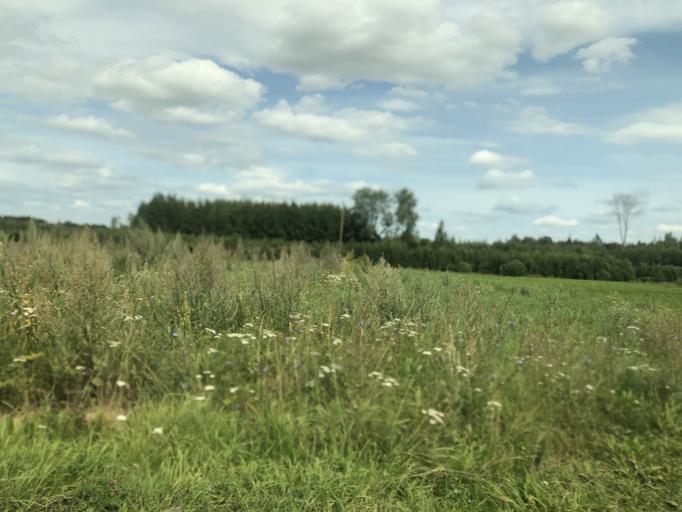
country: LV
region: Vecumnieki
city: Vecumnieki
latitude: 56.4604
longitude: 24.6270
